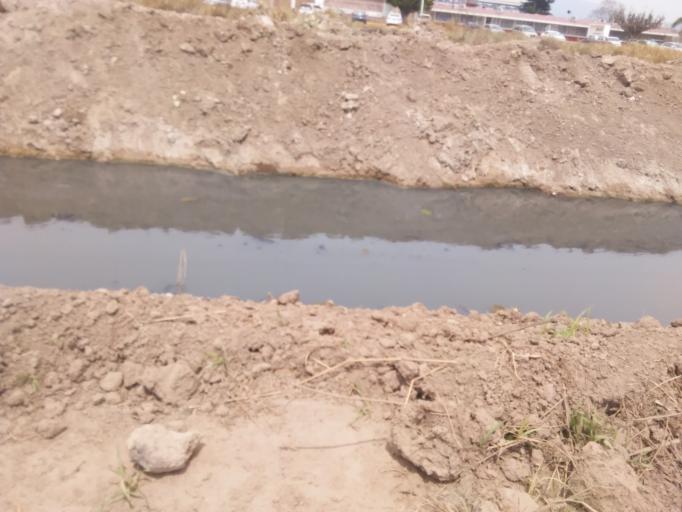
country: MX
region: Nayarit
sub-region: Tepic
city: La Corregidora
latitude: 21.4812
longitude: -104.8430
